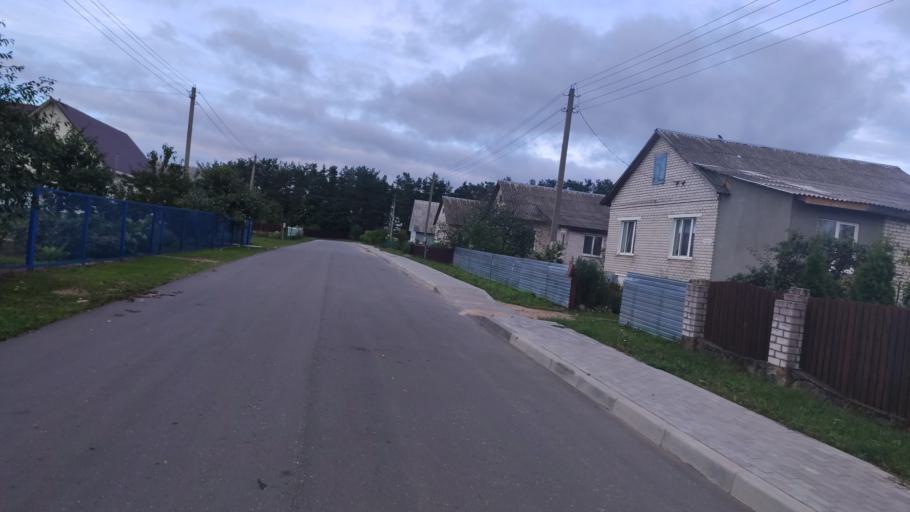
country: BY
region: Minsk
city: Narach
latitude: 54.9319
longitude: 26.6953
